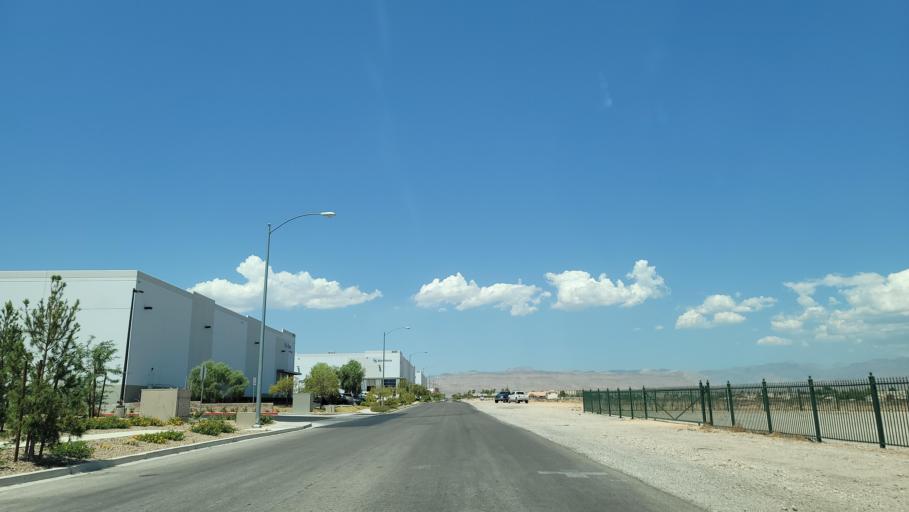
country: US
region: Nevada
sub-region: Clark County
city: Spring Valley
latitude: 36.0744
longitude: -115.2305
